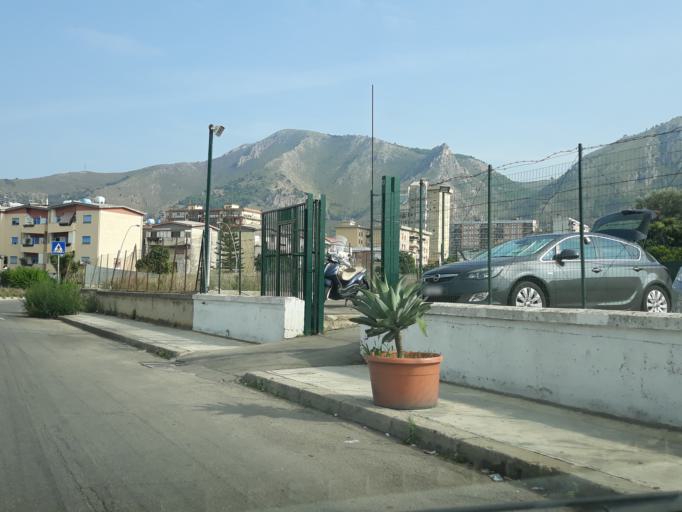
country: IT
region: Sicily
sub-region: Palermo
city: Villa Ciambra
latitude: 38.0850
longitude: 13.3548
